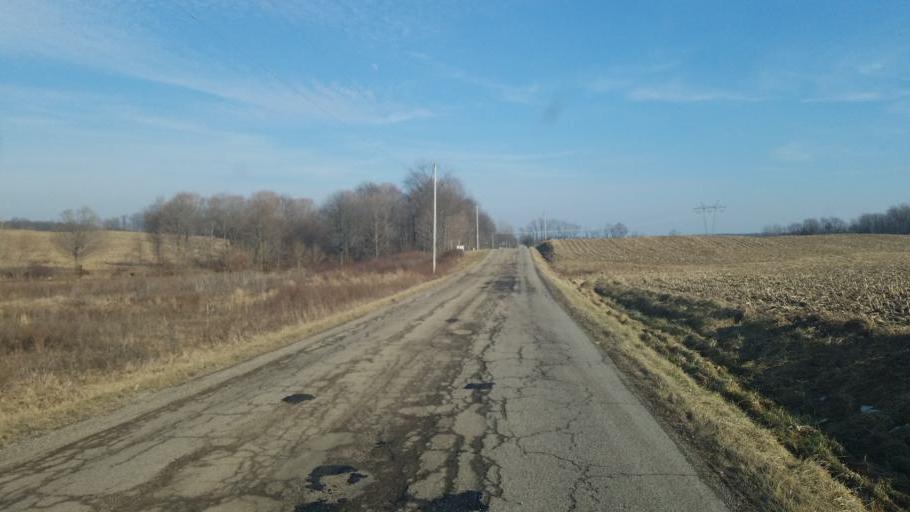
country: US
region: Ohio
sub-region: Richland County
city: Lexington
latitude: 40.6013
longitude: -82.6776
